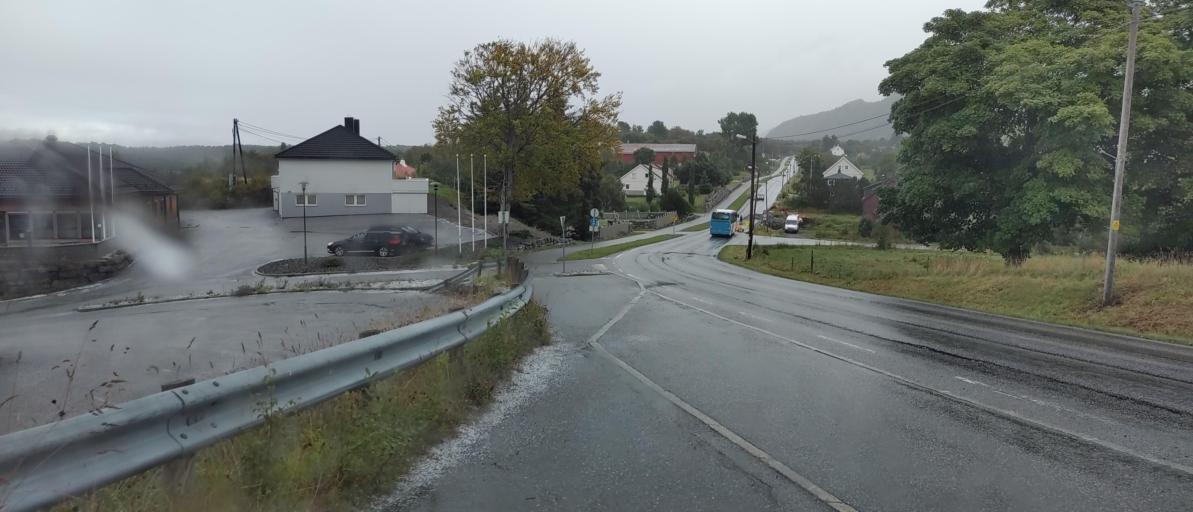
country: NO
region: More og Romsdal
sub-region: Eide
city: Eide
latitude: 63.0151
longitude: 7.4492
